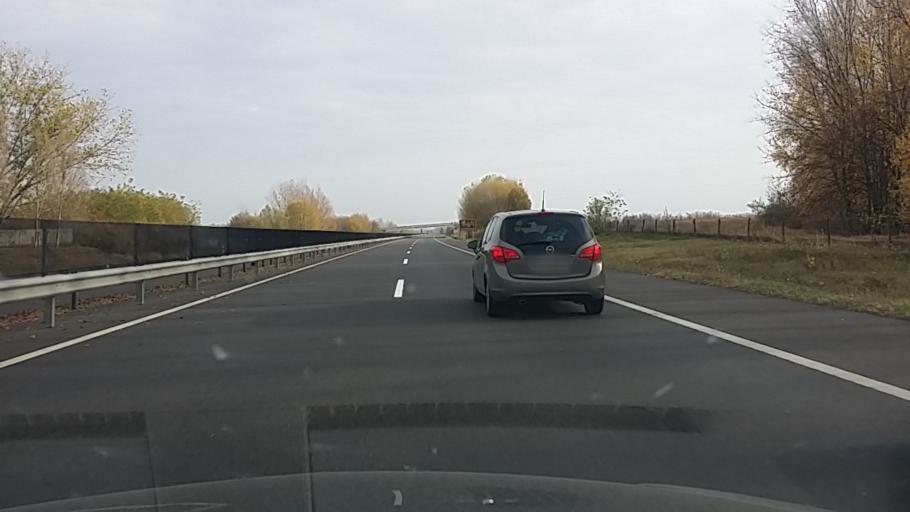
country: HU
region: Szabolcs-Szatmar-Bereg
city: Nyiregyhaza
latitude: 47.8954
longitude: 21.6834
